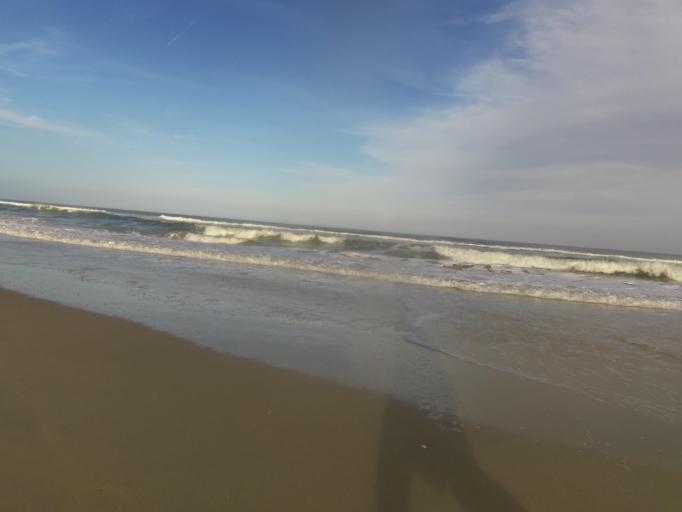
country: US
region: Florida
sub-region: Flagler County
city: Palm Coast
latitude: 29.6241
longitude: -81.1936
